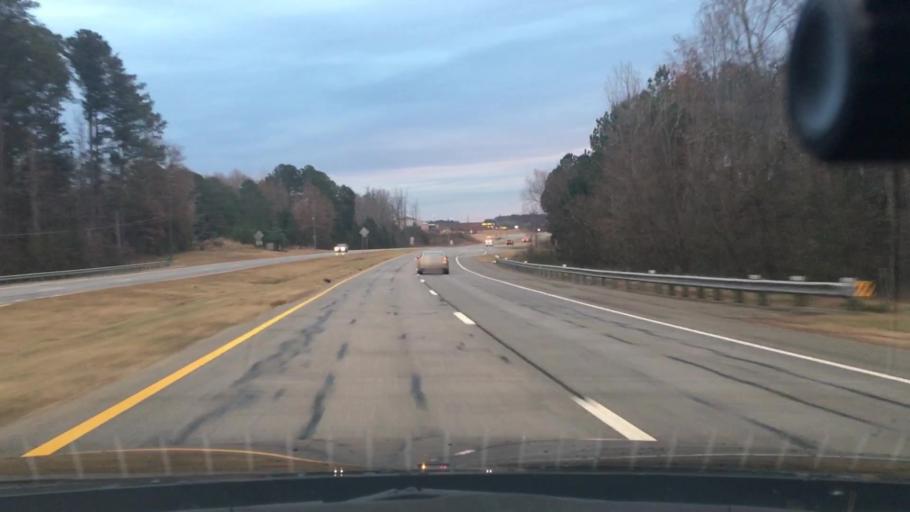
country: US
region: Georgia
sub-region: Fayette County
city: Peachtree City
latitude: 33.4016
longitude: -84.6323
